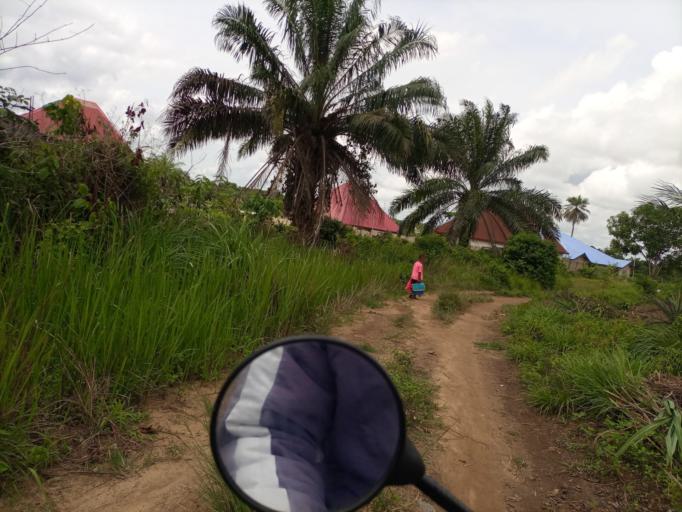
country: SL
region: Southern Province
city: Bo
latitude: 7.9709
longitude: -11.7679
